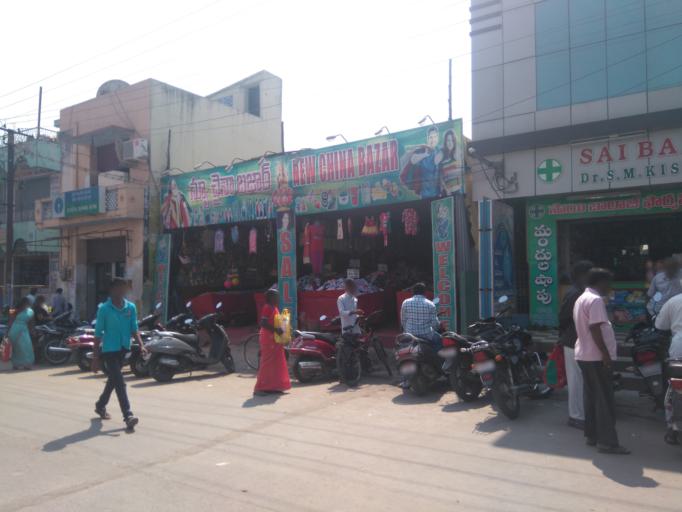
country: IN
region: Andhra Pradesh
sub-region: Chittoor
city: Chittoor
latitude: 13.2173
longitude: 79.0937
